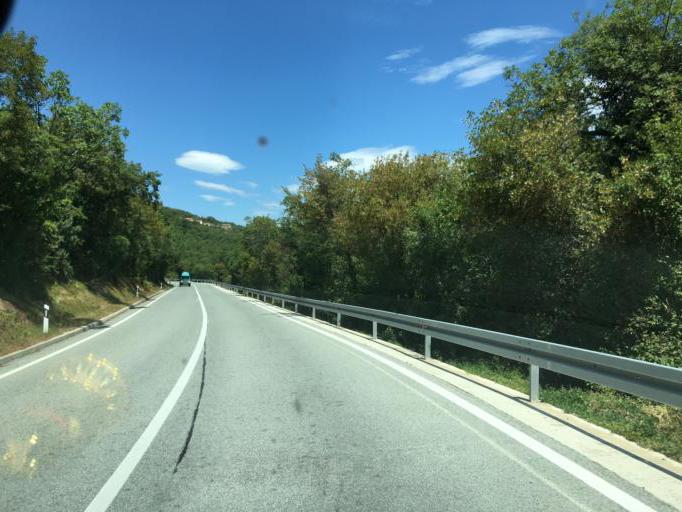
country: HR
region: Istarska
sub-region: Grad Labin
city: Rabac
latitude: 45.1344
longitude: 14.2057
